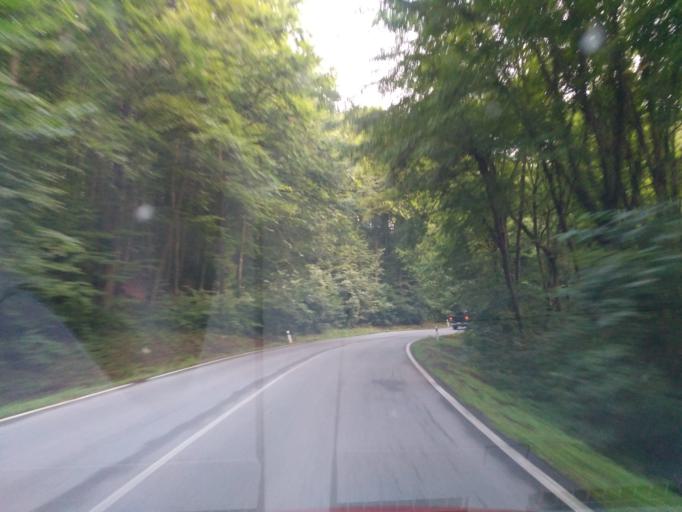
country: SK
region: Presovsky
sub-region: Okres Presov
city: Presov
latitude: 48.9864
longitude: 21.1863
